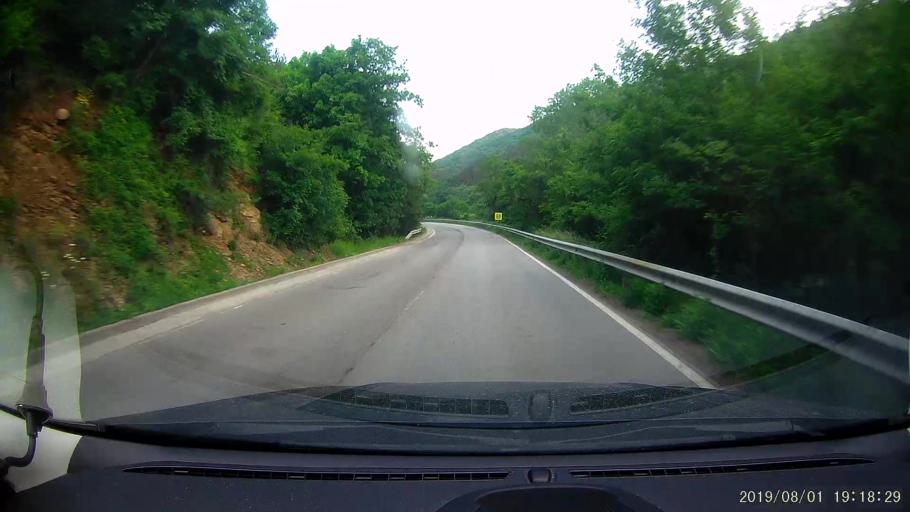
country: BG
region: Shumen
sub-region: Obshtina Smyadovo
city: Smyadovo
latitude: 42.9126
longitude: 26.9400
